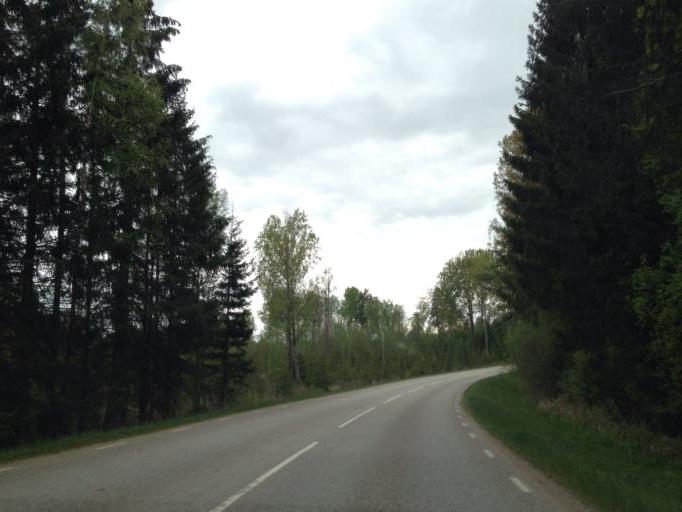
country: SE
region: Soedermanland
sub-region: Eskilstuna Kommun
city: Hallbybrunn
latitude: 59.4044
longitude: 16.3766
